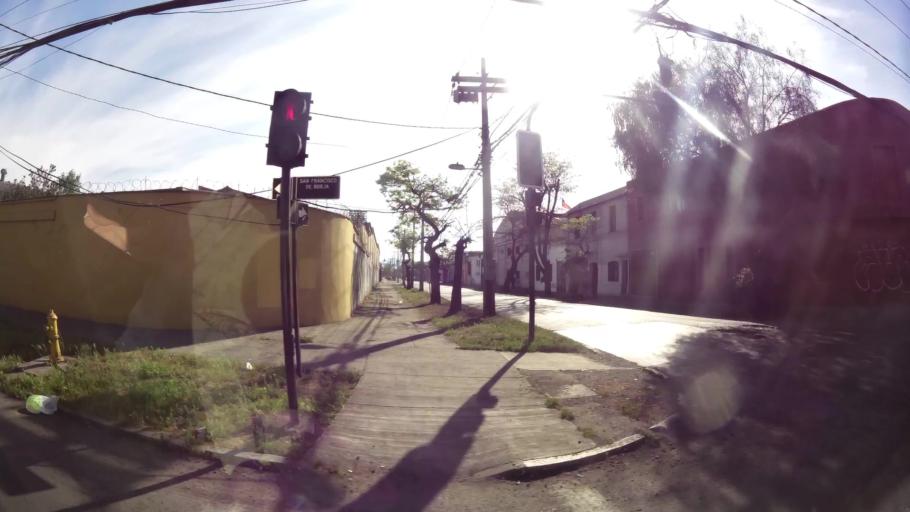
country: CL
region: Santiago Metropolitan
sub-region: Provincia de Santiago
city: Santiago
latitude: -33.4642
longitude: -70.6813
